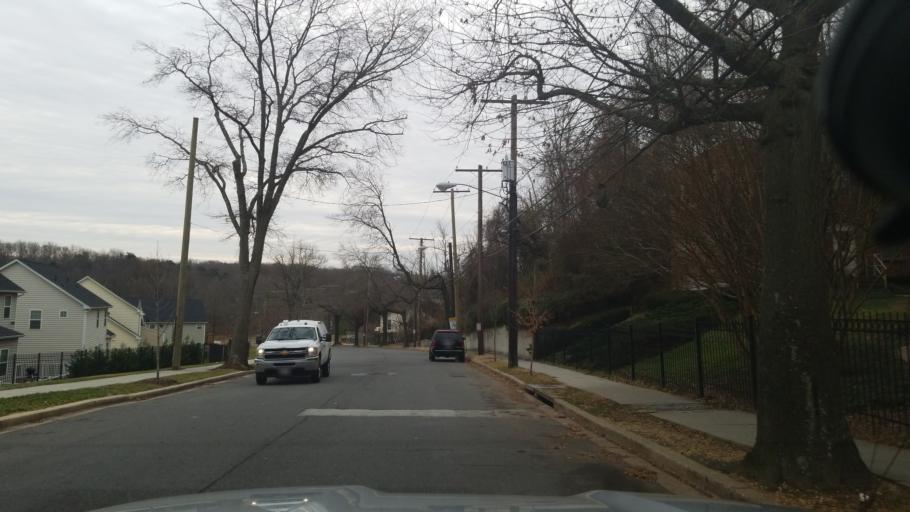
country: US
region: Maryland
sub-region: Prince George's County
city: Hillcrest Heights
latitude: 38.8436
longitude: -76.9834
